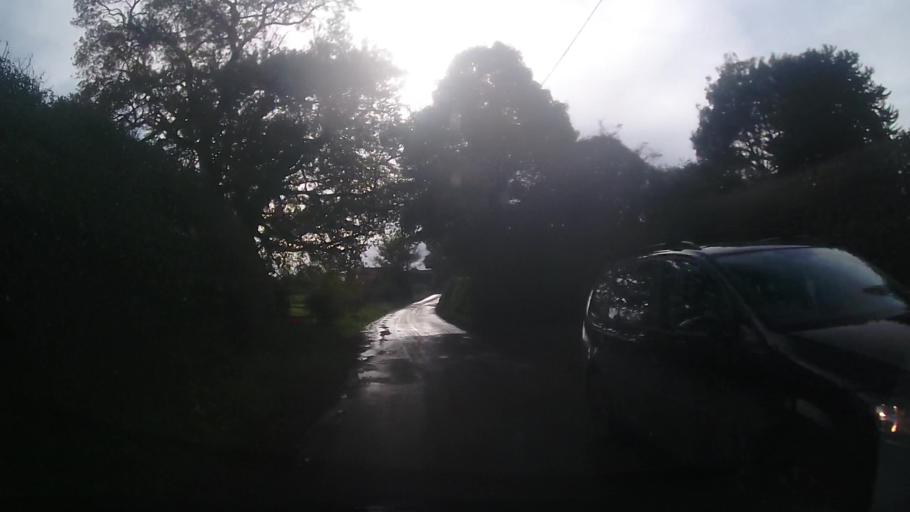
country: GB
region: England
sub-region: Shropshire
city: Whitchurch
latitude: 52.9544
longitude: -2.6963
